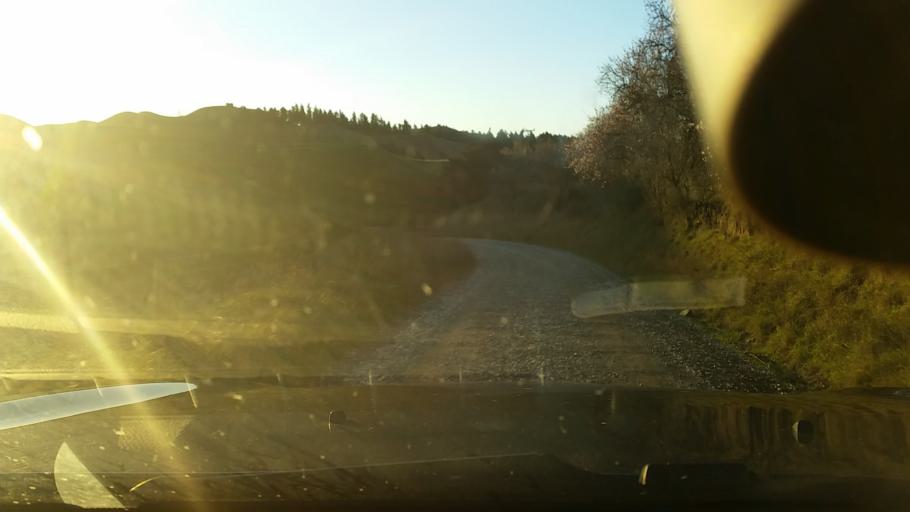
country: NZ
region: Marlborough
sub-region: Marlborough District
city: Blenheim
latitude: -41.7319
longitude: 174.0370
